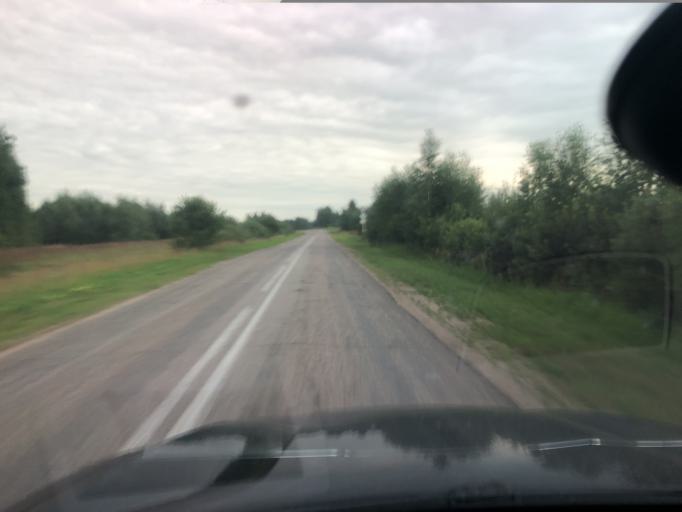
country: RU
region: Jaroslavl
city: Petrovsk
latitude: 57.0011
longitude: 39.0414
